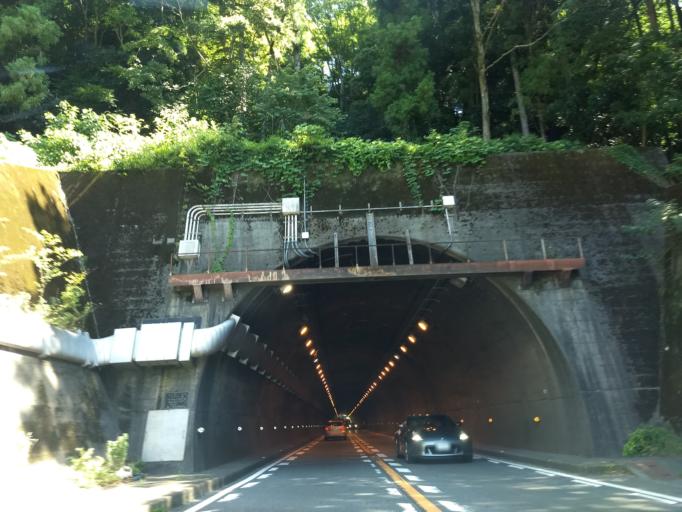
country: JP
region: Shizuoka
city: Gotemba
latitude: 35.3597
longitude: 138.9747
